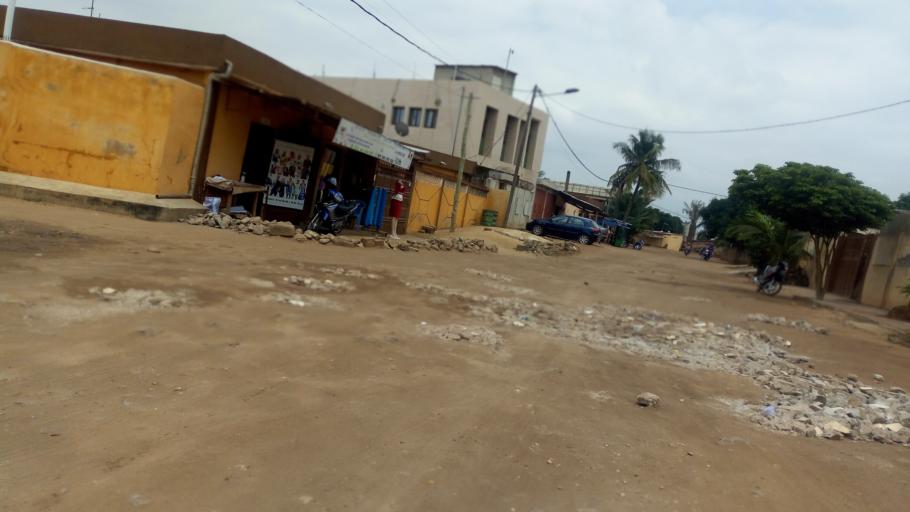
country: TG
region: Maritime
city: Lome
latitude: 6.1859
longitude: 1.1884
